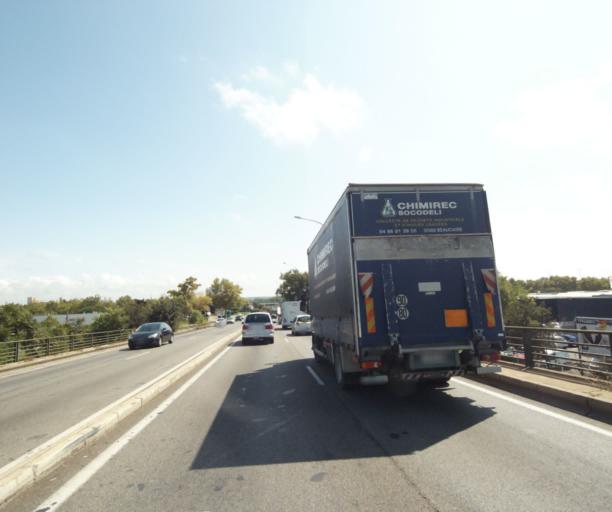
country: FR
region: Languedoc-Roussillon
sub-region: Departement du Gard
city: Nimes
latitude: 43.8173
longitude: 4.3391
